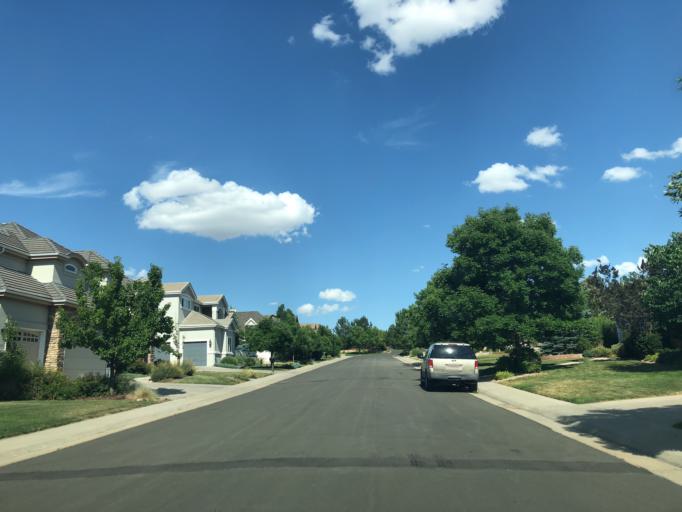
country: US
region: Colorado
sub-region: Arapahoe County
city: Dove Valley
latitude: 39.5959
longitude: -104.7803
